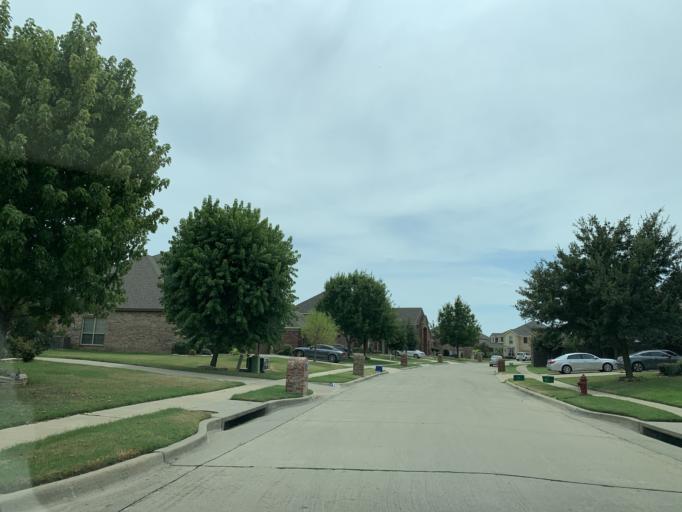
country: US
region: Texas
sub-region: Dallas County
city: Grand Prairie
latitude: 32.6537
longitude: -97.0378
